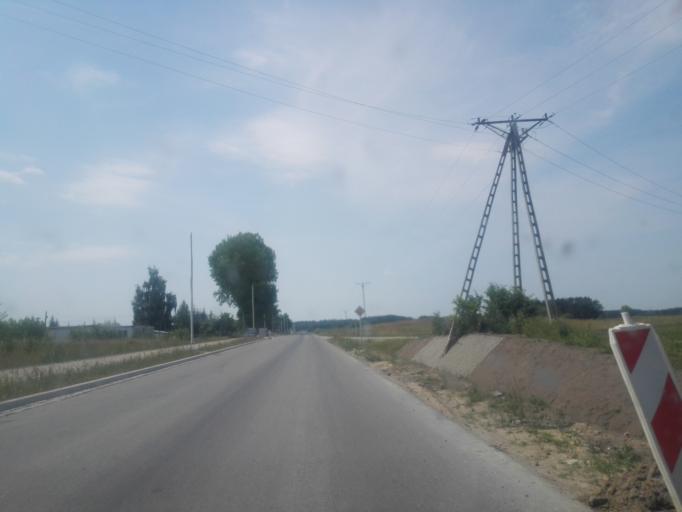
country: PL
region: Podlasie
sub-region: Powiat sejnenski
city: Krasnopol
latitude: 54.0806
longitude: 23.0730
